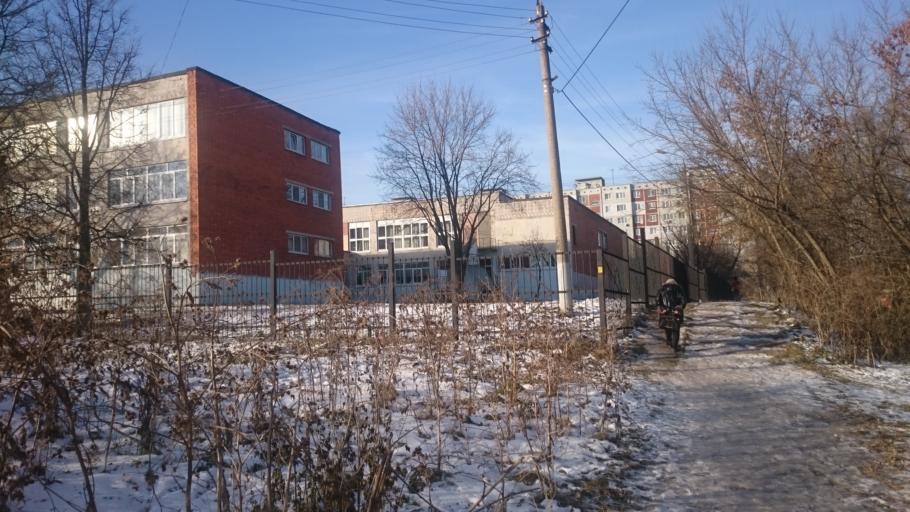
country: RU
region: Tula
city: Tula
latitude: 54.1773
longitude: 37.6376
